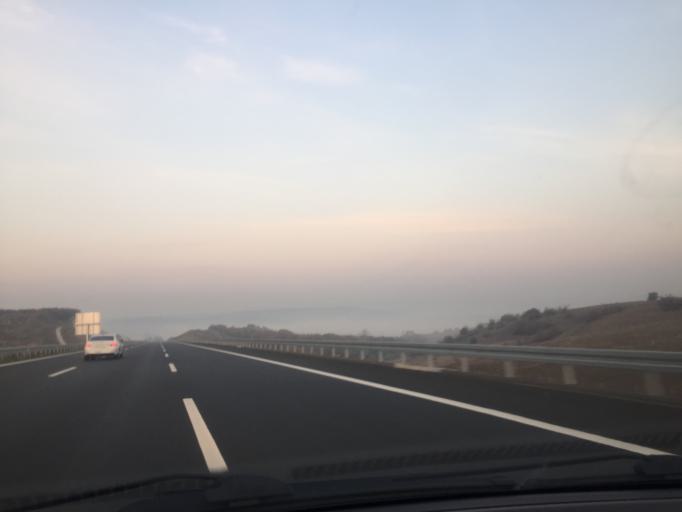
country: TR
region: Bursa
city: Mahmudiye
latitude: 40.2596
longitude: 28.6835
